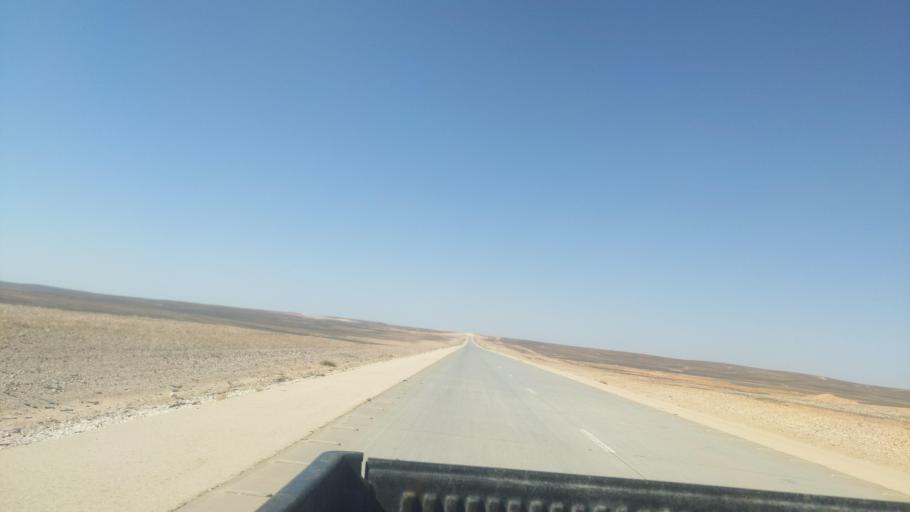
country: JO
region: Amman
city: Al Azraq ash Shamali
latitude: 31.4112
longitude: 36.7184
